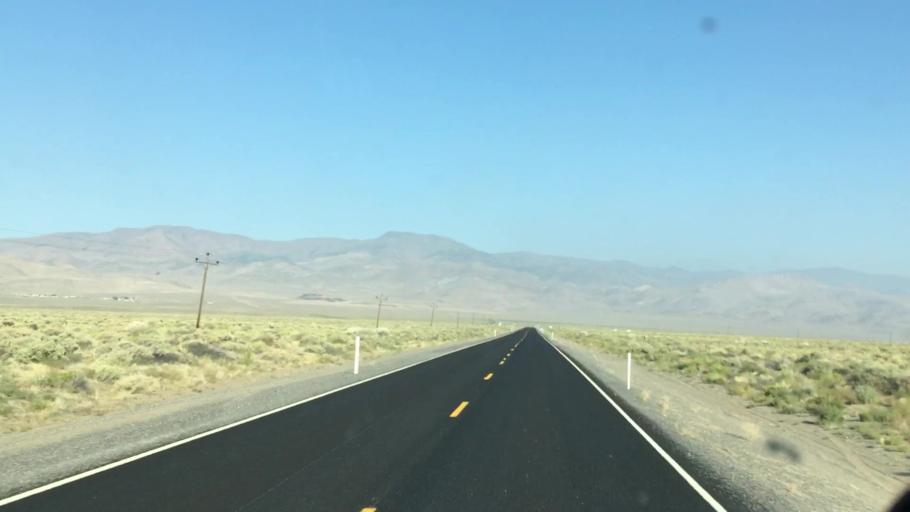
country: US
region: Nevada
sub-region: Lyon County
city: Fernley
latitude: 39.6463
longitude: -119.3130
